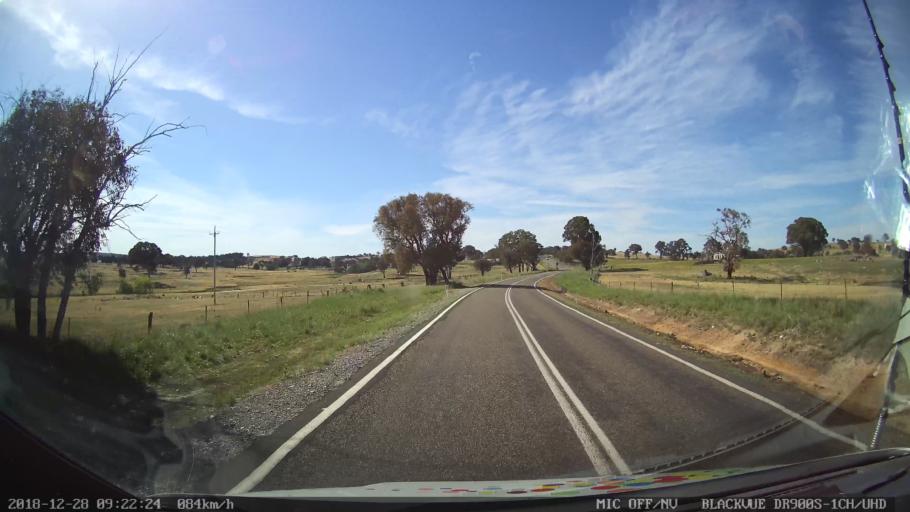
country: AU
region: New South Wales
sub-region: Upper Lachlan Shire
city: Crookwell
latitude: -34.3733
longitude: 149.3817
